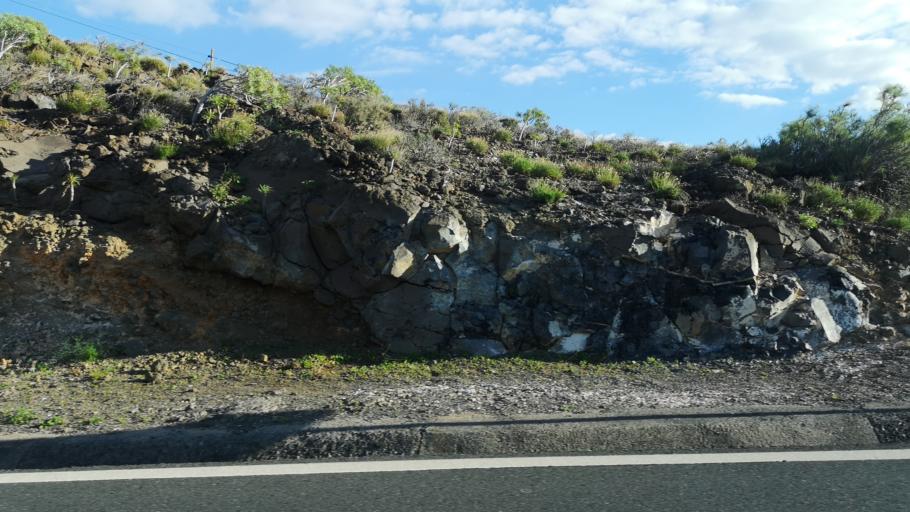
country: ES
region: Canary Islands
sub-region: Provincia de Santa Cruz de Tenerife
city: San Sebastian de la Gomera
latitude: 28.0843
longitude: -17.1252
